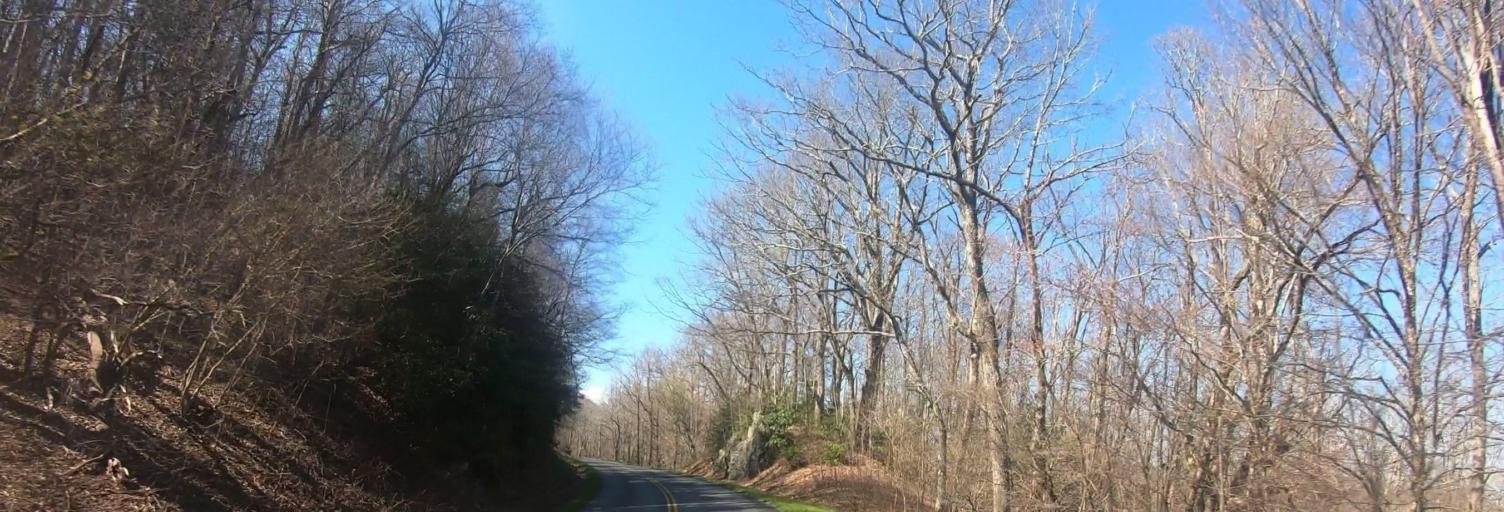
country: US
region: North Carolina
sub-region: Avery County
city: Newland
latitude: 36.0435
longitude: -81.8633
